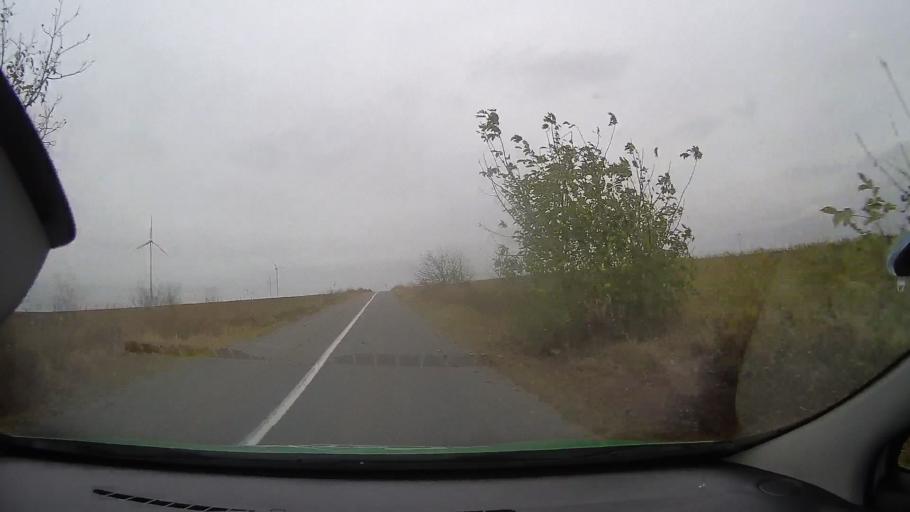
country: RO
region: Constanta
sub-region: Comuna Pantelimon
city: Pantelimon
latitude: 44.5032
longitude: 28.3504
